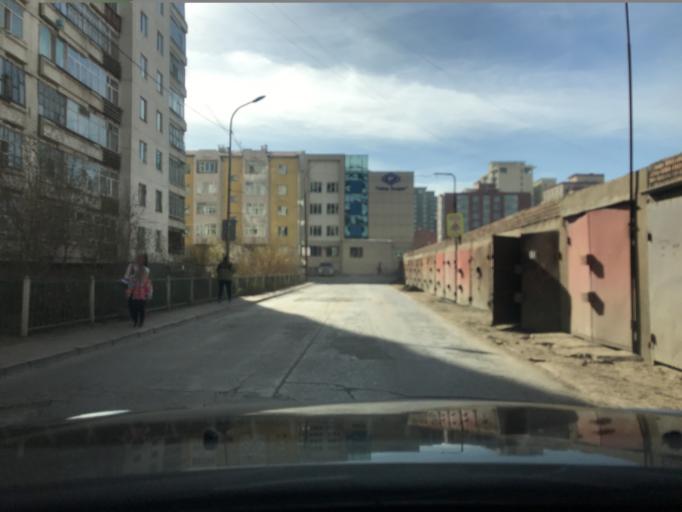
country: MN
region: Ulaanbaatar
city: Ulaanbaatar
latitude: 47.9121
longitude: 106.9401
